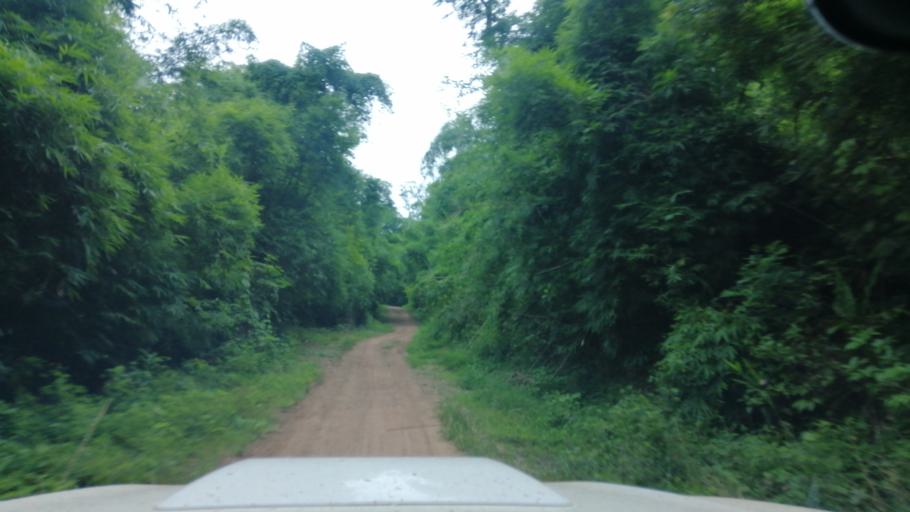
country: TH
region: Nan
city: Mae Charim
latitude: 18.7663
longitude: 101.3062
